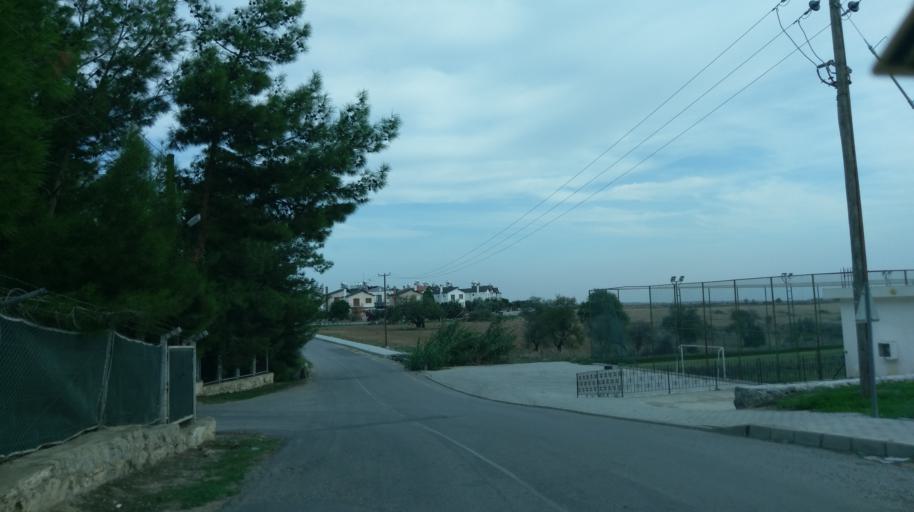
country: CY
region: Keryneia
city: Kyrenia
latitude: 35.2659
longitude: 33.3307
